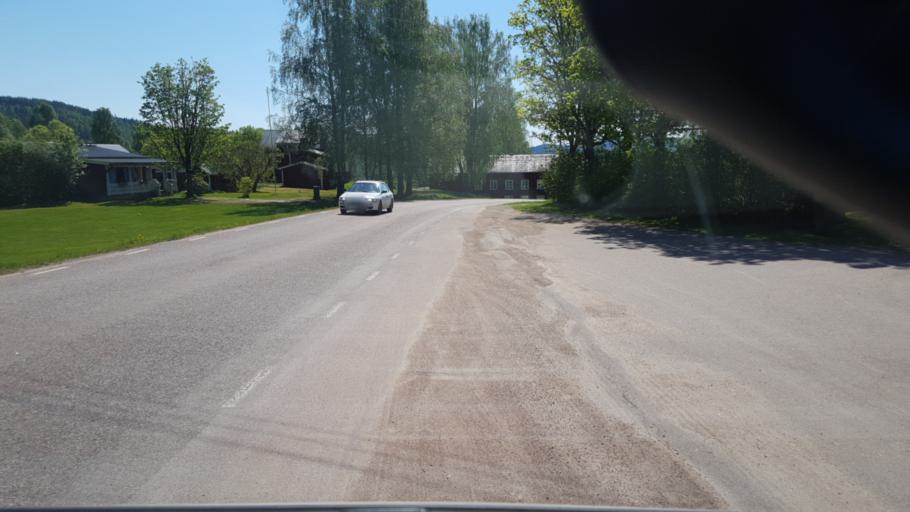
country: SE
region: Vaermland
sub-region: Arvika Kommun
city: Arvika
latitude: 59.7531
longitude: 12.8235
